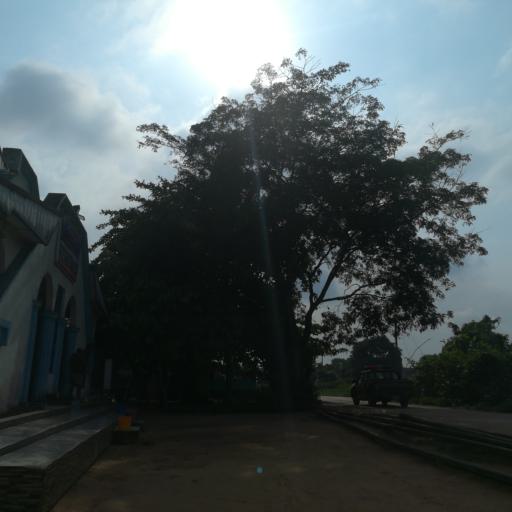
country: NG
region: Rivers
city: Okrika
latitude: 4.7823
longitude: 7.1441
